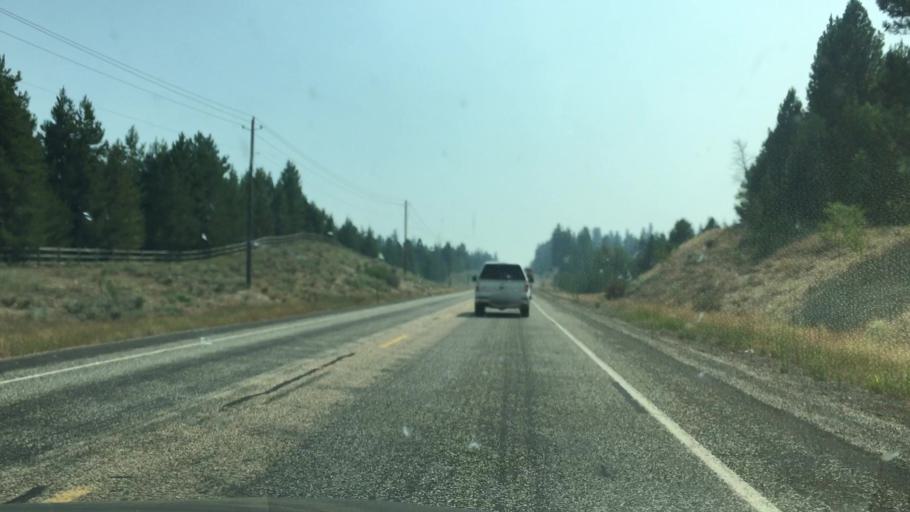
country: US
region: Idaho
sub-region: Valley County
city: Cascade
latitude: 44.3843
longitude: -116.0124
